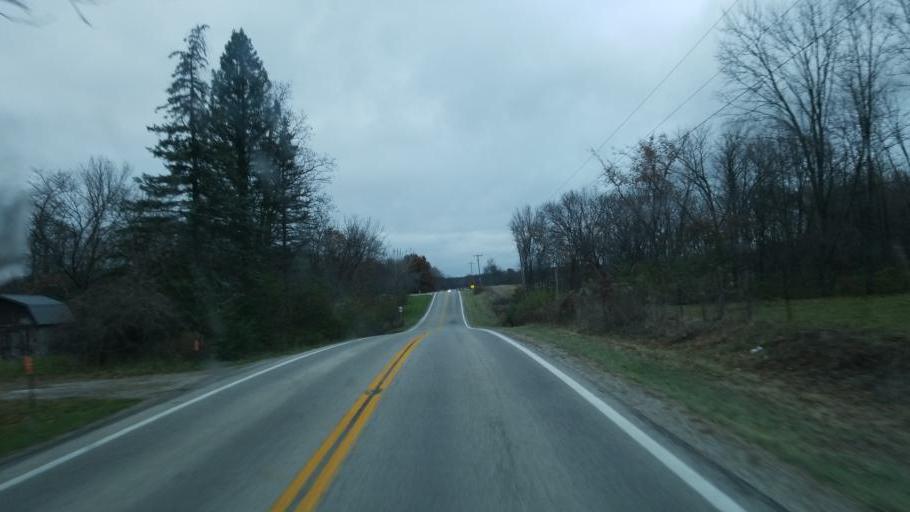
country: US
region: Ohio
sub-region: Morrow County
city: Mount Gilead
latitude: 40.4901
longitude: -82.8202
